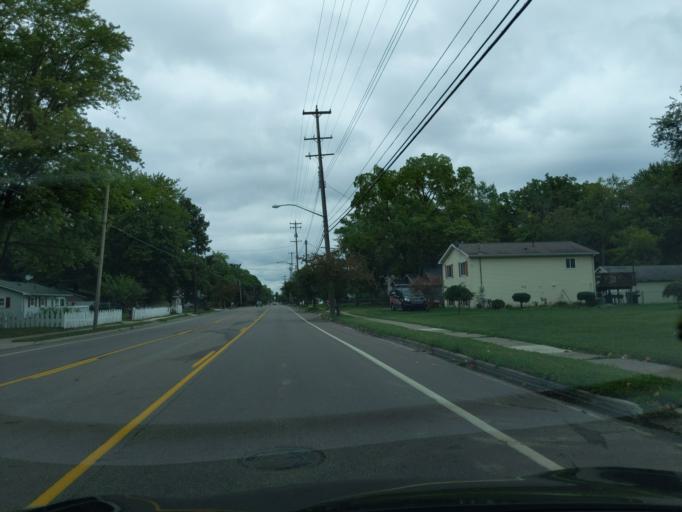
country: US
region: Michigan
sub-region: Ingham County
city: Lansing
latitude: 42.6831
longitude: -84.5899
